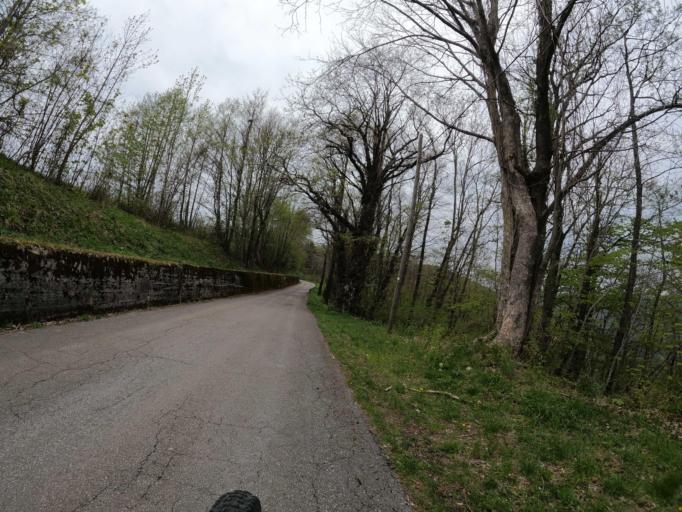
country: IT
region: Friuli Venezia Giulia
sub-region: Provincia di Udine
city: Clodig
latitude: 46.1446
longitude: 13.6088
